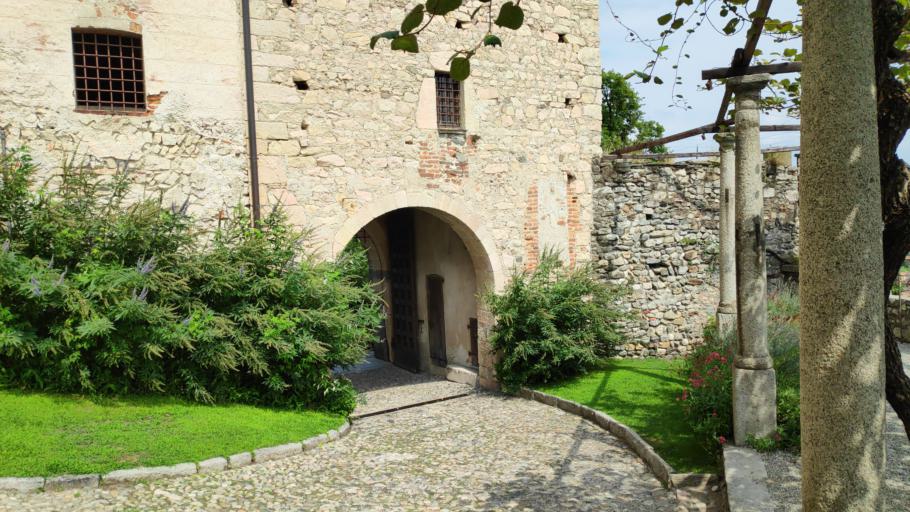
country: IT
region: Lombardy
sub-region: Provincia di Varese
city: Angera
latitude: 45.7740
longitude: 8.5718
